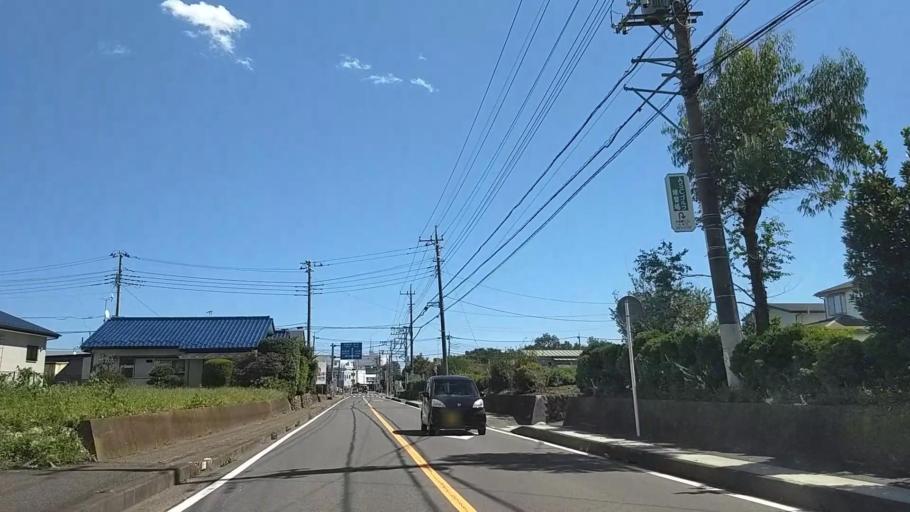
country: JP
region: Kanagawa
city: Zama
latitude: 35.5310
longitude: 139.3178
